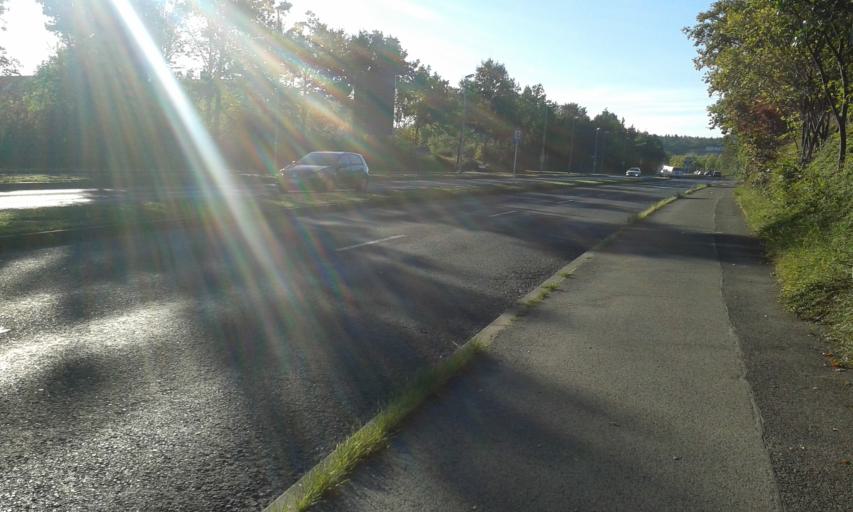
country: DE
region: Bavaria
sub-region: Upper Franconia
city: Bamberg
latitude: 49.8729
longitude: 10.8892
